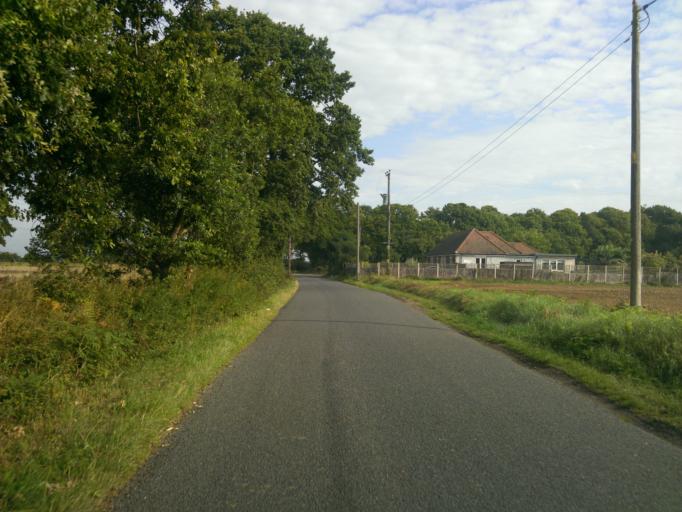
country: GB
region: England
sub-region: Essex
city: Little Clacton
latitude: 51.8392
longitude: 1.1046
